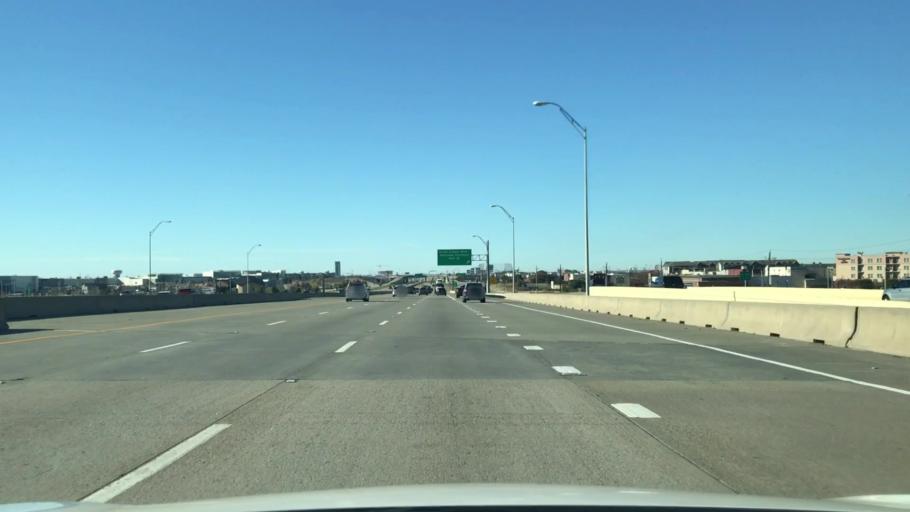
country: US
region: Texas
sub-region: Denton County
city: The Colony
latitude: 33.0809
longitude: -96.8560
